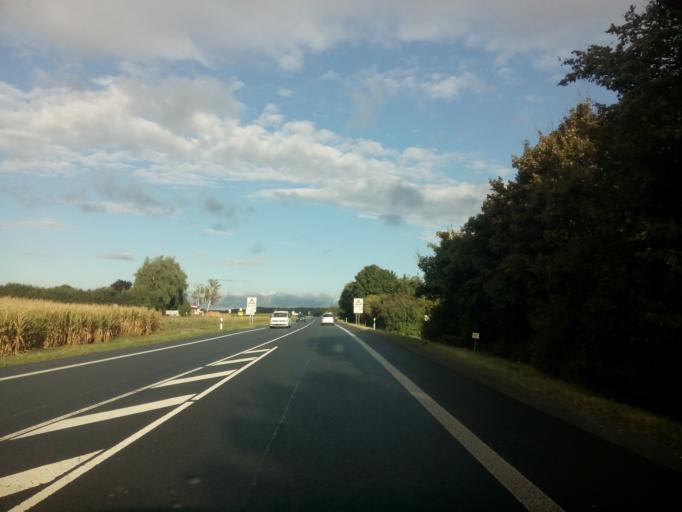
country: DE
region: Hesse
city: Gross-Umstadt
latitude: 49.8735
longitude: 8.9113
